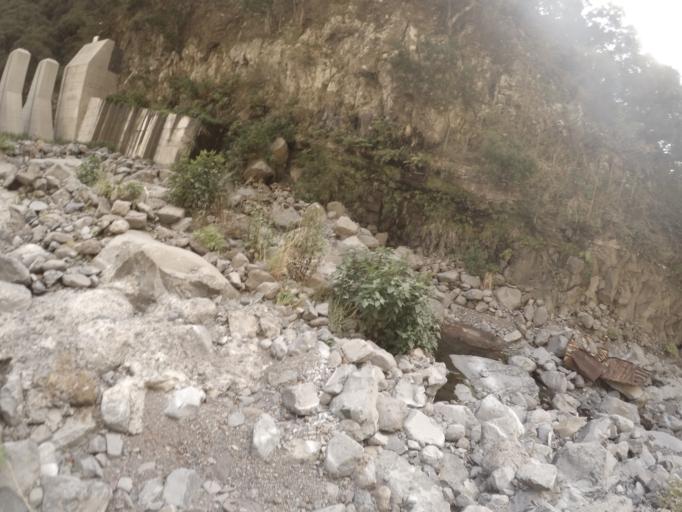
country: PT
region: Madeira
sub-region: Funchal
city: Nossa Senhora do Monte
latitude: 32.6984
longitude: -16.9194
